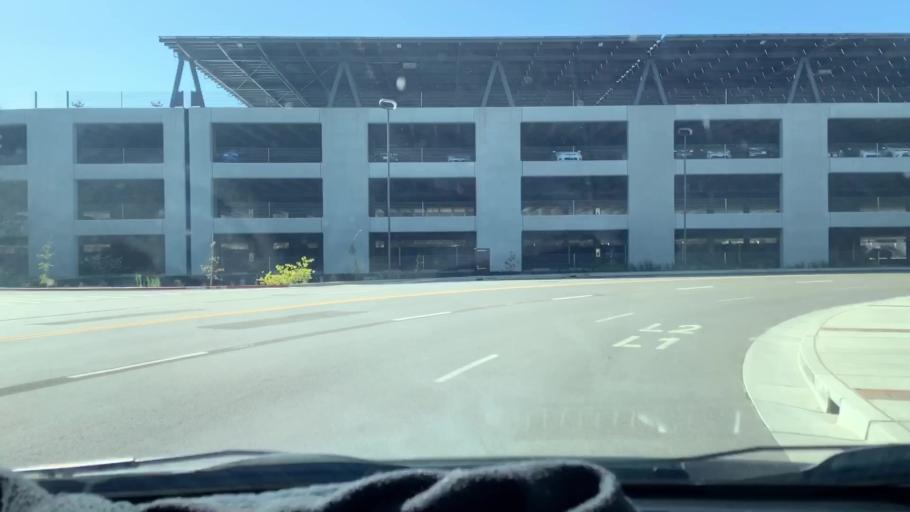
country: US
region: California
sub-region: Santa Clara County
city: Cupertino
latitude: 37.3289
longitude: -122.0079
